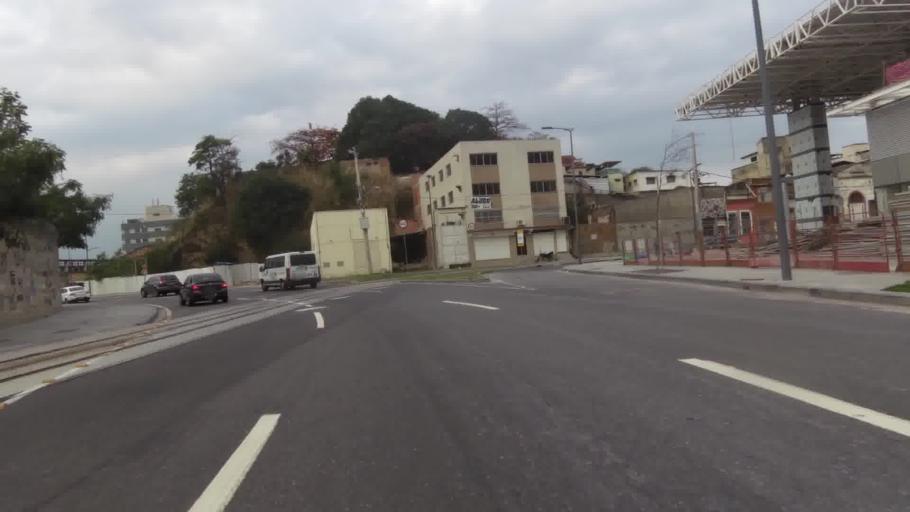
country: BR
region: Rio de Janeiro
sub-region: Rio De Janeiro
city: Rio de Janeiro
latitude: -22.8966
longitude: -43.2015
